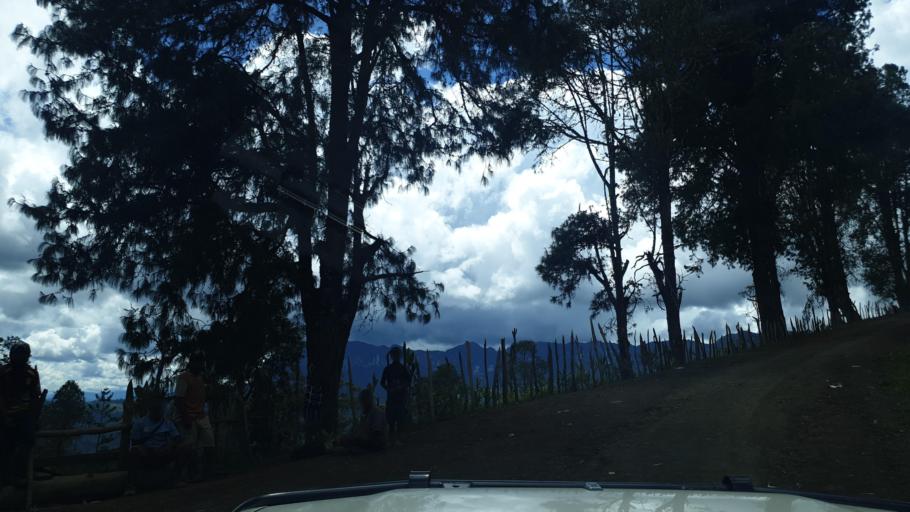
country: PG
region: Eastern Highlands
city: Goroka
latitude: -6.2777
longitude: 145.1859
